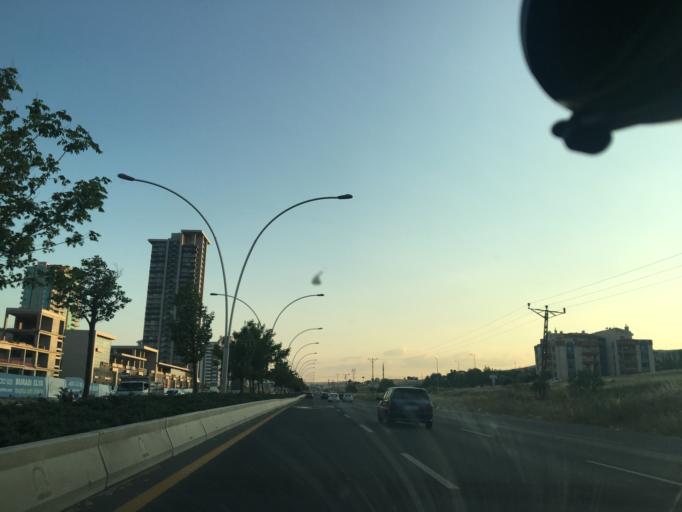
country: TR
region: Ankara
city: Etimesgut
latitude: 39.8769
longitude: 32.6520
